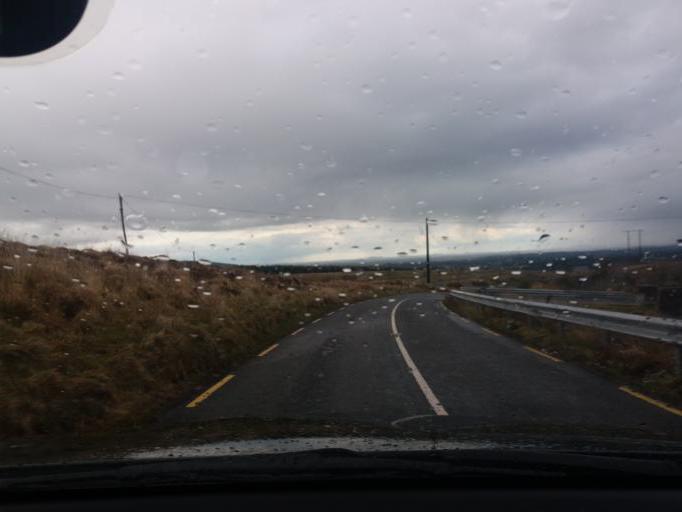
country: IE
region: Ulster
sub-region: An Cabhan
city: Ballyconnell
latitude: 54.1636
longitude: -7.7859
